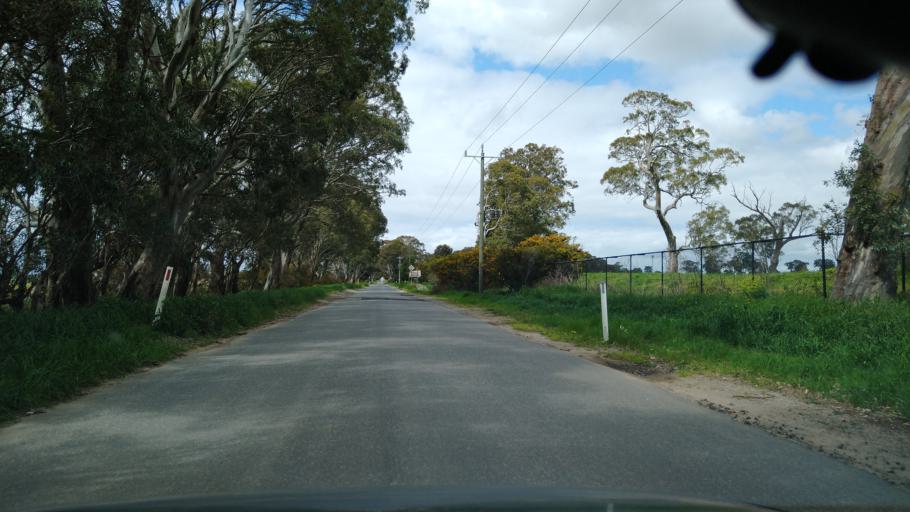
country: AU
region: Victoria
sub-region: Frankston
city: Sandhurst
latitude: -38.0609
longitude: 145.2268
